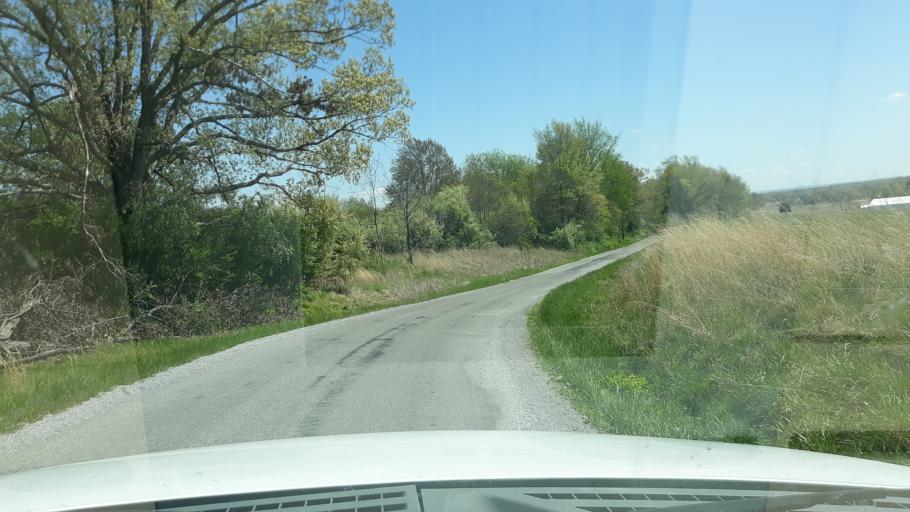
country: US
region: Illinois
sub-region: Saline County
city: Harrisburg
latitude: 37.8554
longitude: -88.6347
